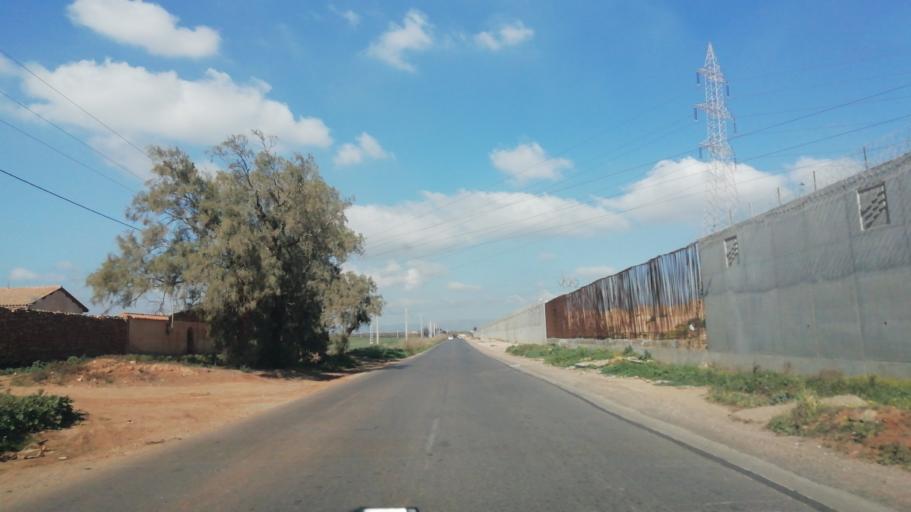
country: DZ
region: Oran
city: Ain el Bya
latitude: 35.7520
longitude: -0.2669
